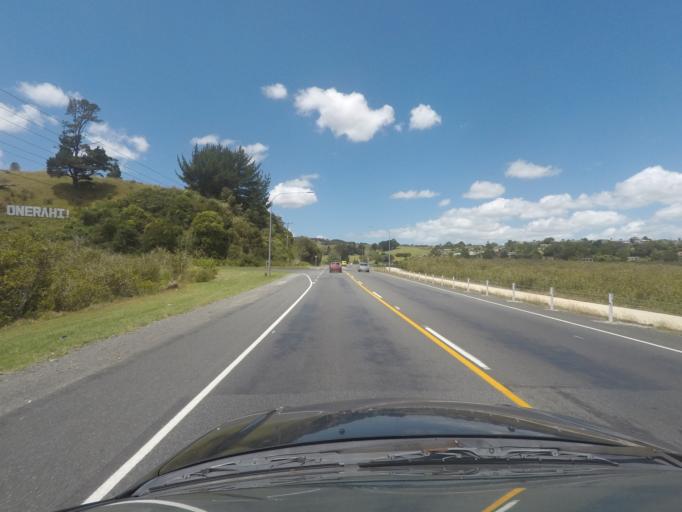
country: NZ
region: Northland
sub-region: Whangarei
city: Whangarei
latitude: -35.7384
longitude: 174.3585
